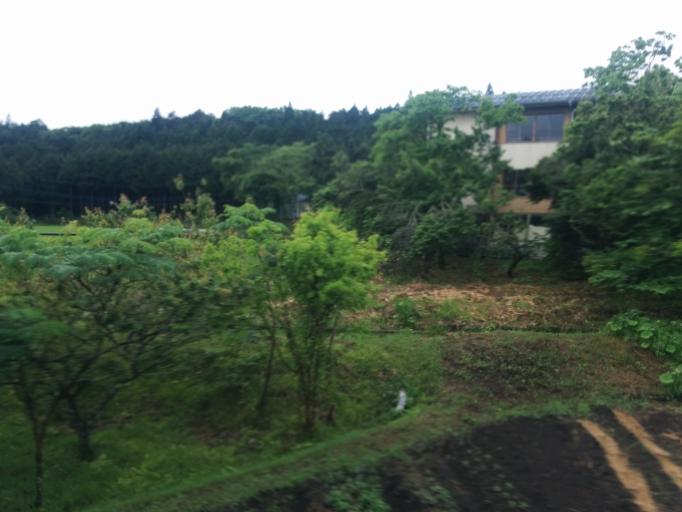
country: JP
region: Tochigi
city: Nikko
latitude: 36.7344
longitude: 139.6484
